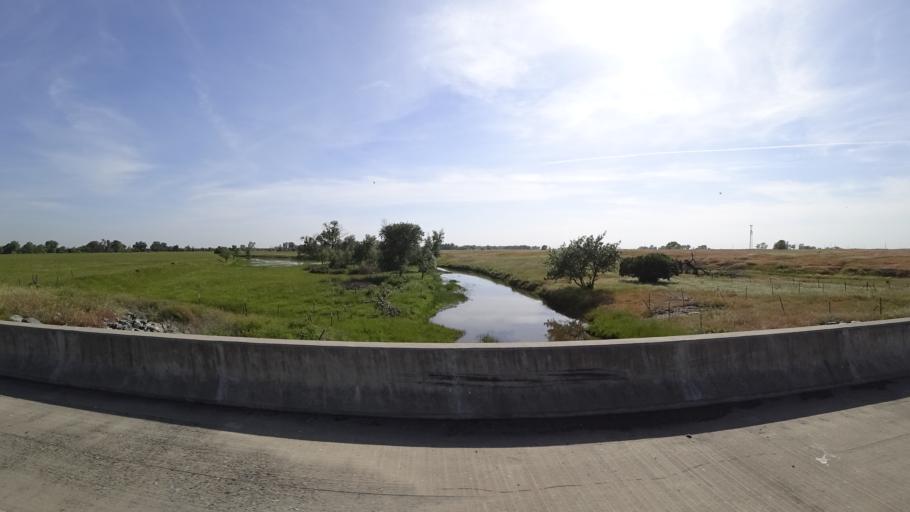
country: US
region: California
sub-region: Butte County
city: Durham
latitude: 39.6126
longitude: -121.6784
